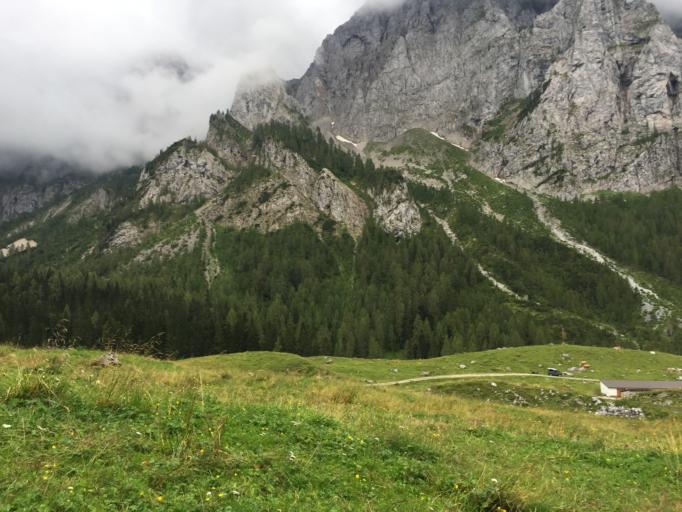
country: IT
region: Friuli Venezia Giulia
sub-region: Provincia di Udine
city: Forni Avoltri
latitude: 46.5633
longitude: 12.7649
